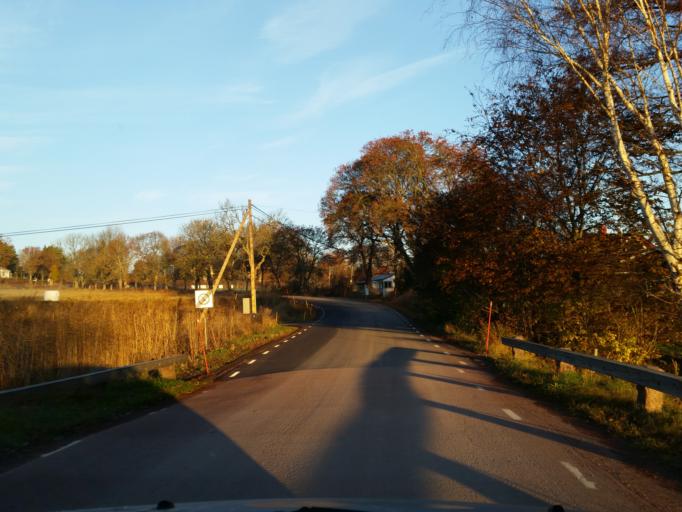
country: AX
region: Alands landsbygd
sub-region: Sund
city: Sund
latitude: 60.2337
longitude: 20.0802
